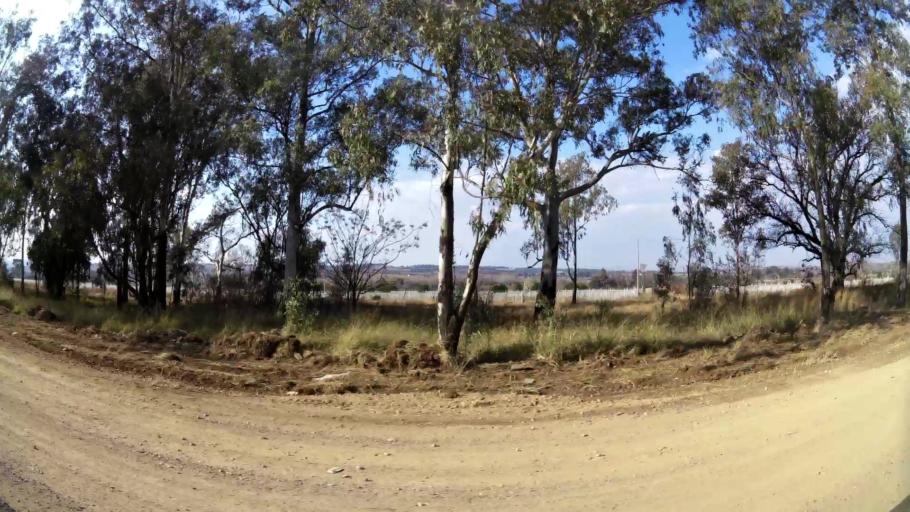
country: ZA
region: Gauteng
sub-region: Ekurhuleni Metropolitan Municipality
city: Tembisa
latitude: -25.9299
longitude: 28.2317
